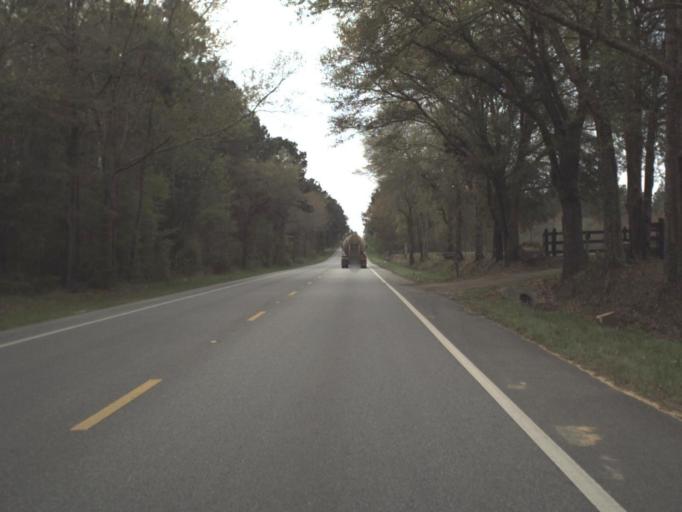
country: US
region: Florida
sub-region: Holmes County
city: Bonifay
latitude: 30.8447
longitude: -85.6668
